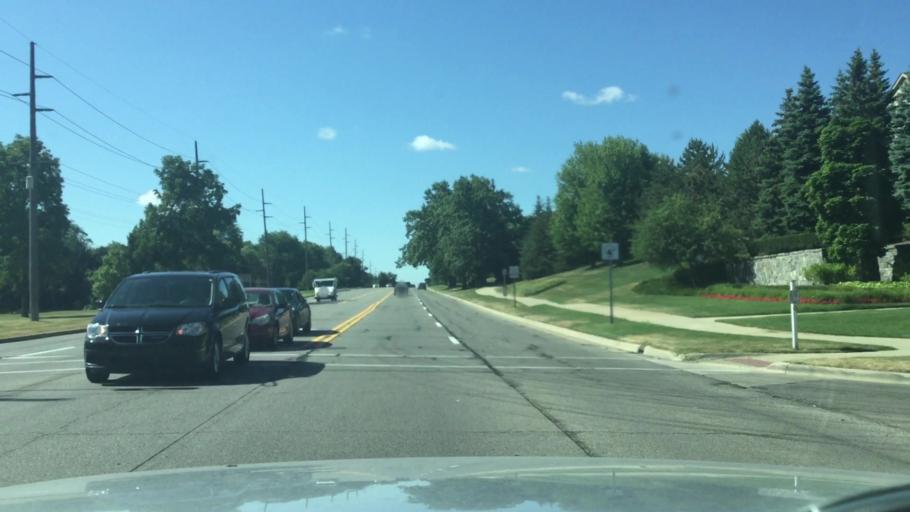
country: US
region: Michigan
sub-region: Oakland County
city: West Bloomfield Township
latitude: 42.5574
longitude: -83.3614
